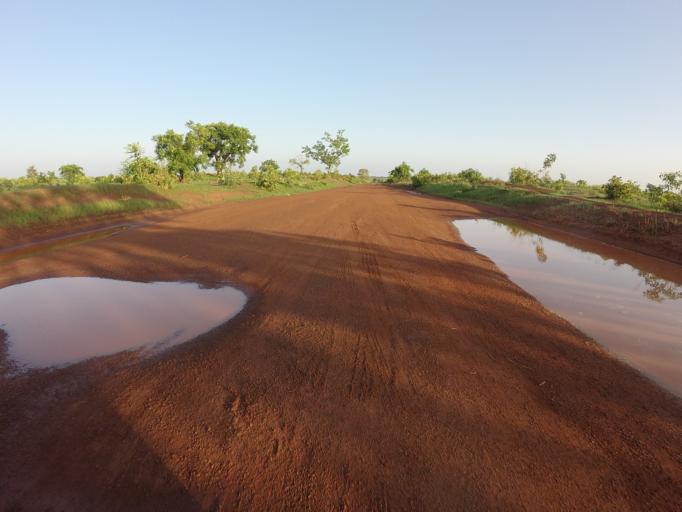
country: TG
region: Savanes
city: Sansanne-Mango
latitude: 10.2610
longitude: -0.0796
